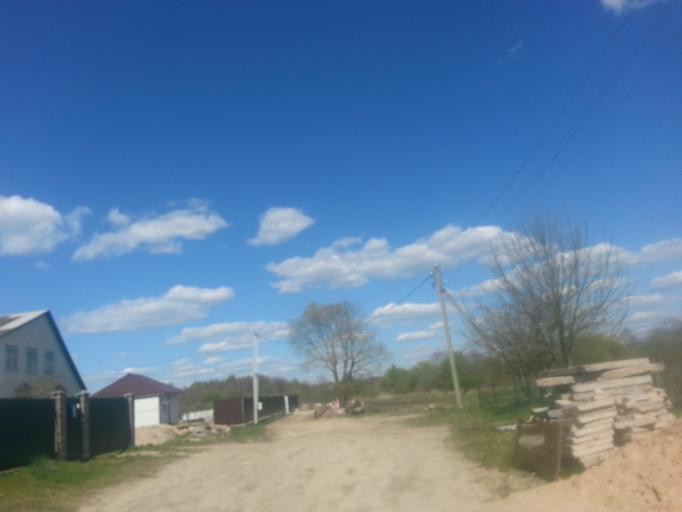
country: BY
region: Minsk
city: Narach
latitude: 54.9430
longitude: 26.6884
